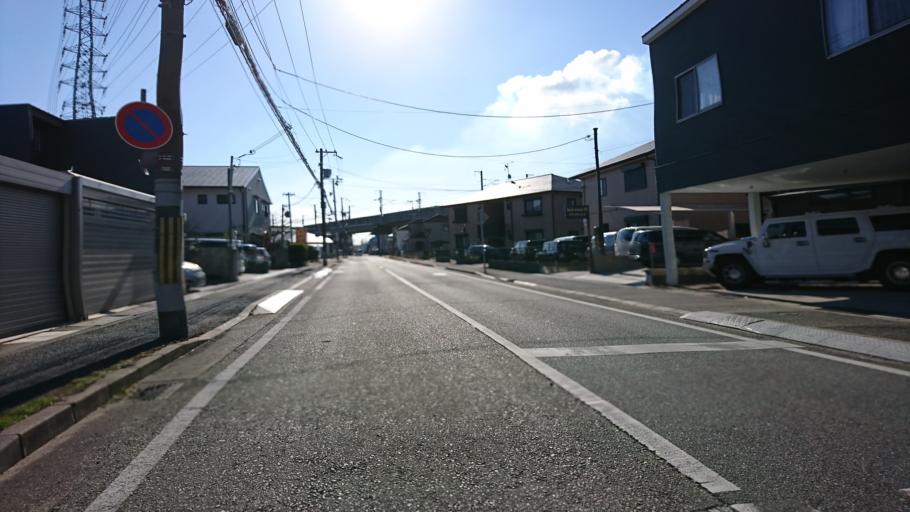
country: JP
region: Hyogo
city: Kakogawacho-honmachi
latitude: 34.7365
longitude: 134.8433
